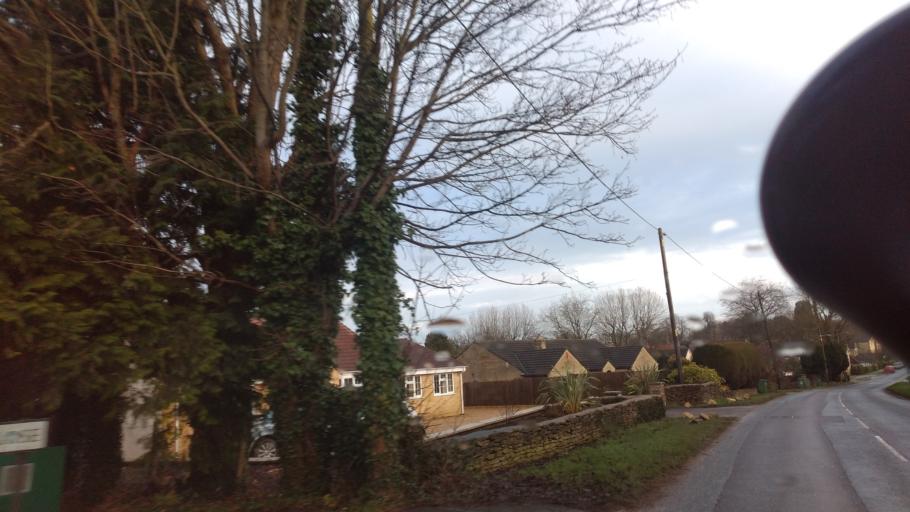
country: GB
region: England
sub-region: Wiltshire
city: Neston
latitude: 51.4314
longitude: -2.2060
